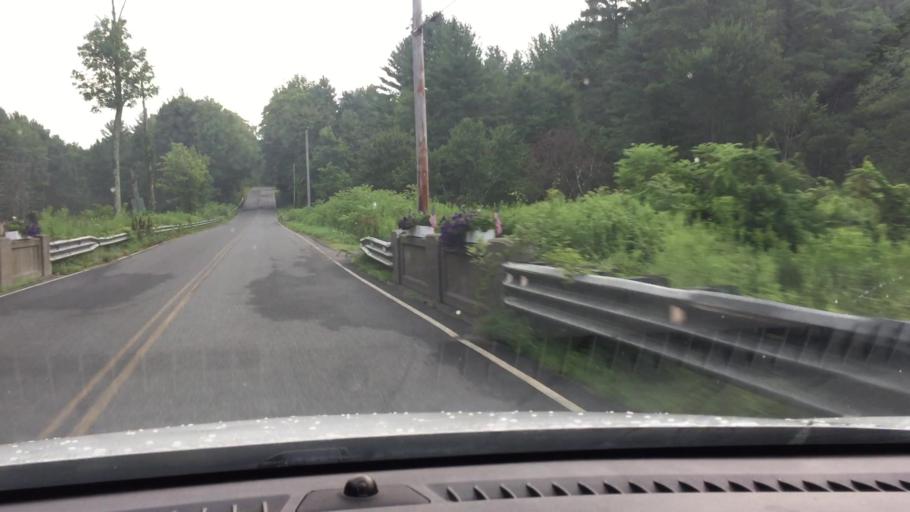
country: US
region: Massachusetts
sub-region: Hampshire County
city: Westhampton
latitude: 42.2630
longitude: -72.9100
